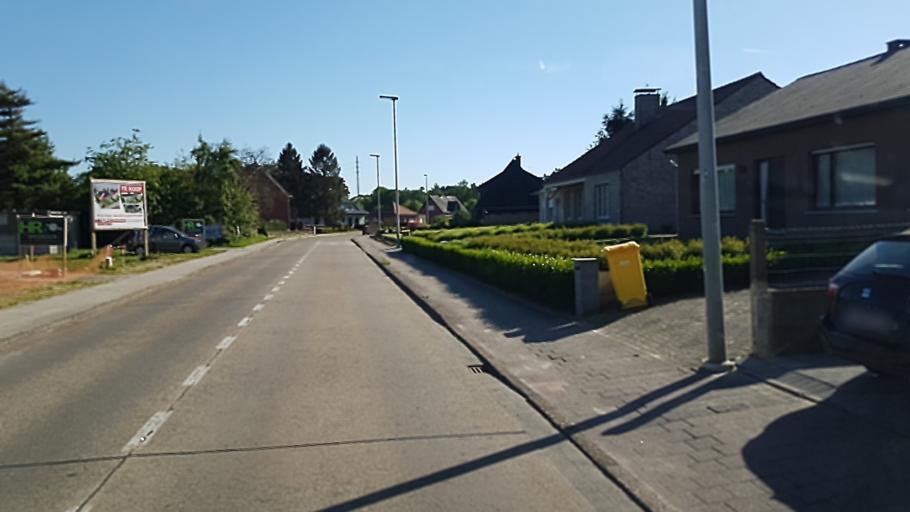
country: BE
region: Flanders
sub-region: Provincie Antwerpen
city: Herentals
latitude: 51.1617
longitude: 4.8215
